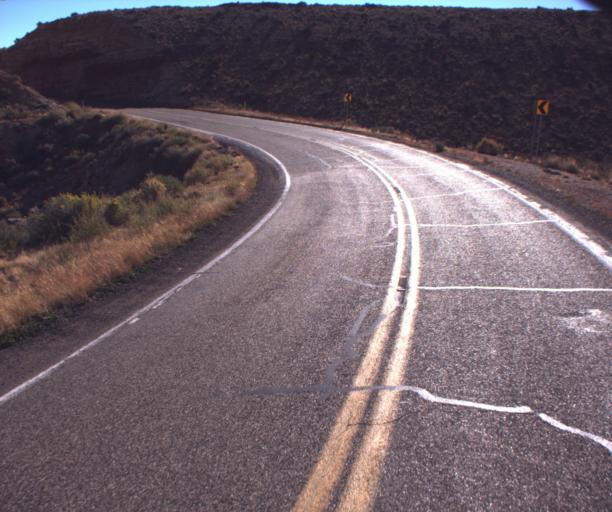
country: US
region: Arizona
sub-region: Coconino County
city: Fredonia
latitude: 36.7328
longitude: -112.0619
